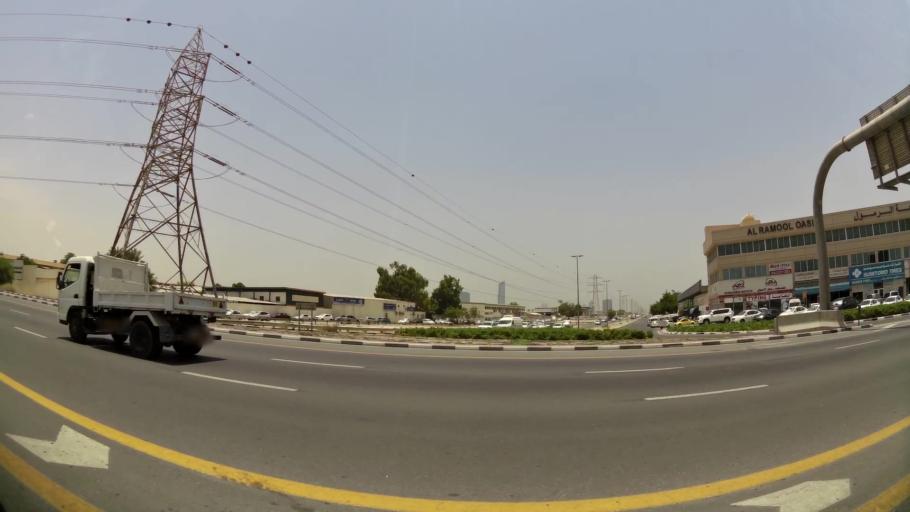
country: AE
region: Ash Shariqah
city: Sharjah
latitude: 25.2219
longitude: 55.3763
